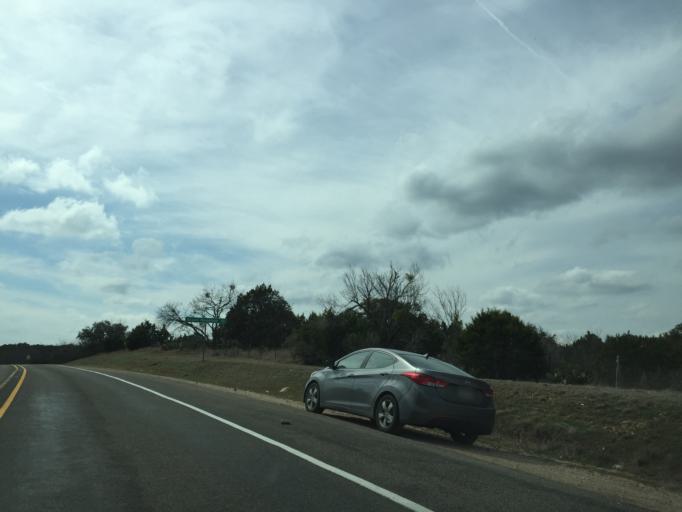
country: US
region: Texas
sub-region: Burnet County
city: Granite Shoals
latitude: 30.5360
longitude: -98.4436
